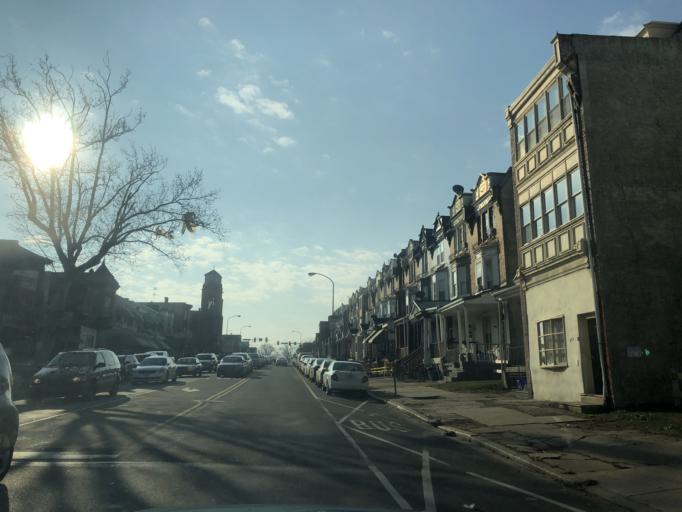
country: US
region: Pennsylvania
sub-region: Delaware County
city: Millbourne
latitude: 39.9681
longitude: -75.2252
